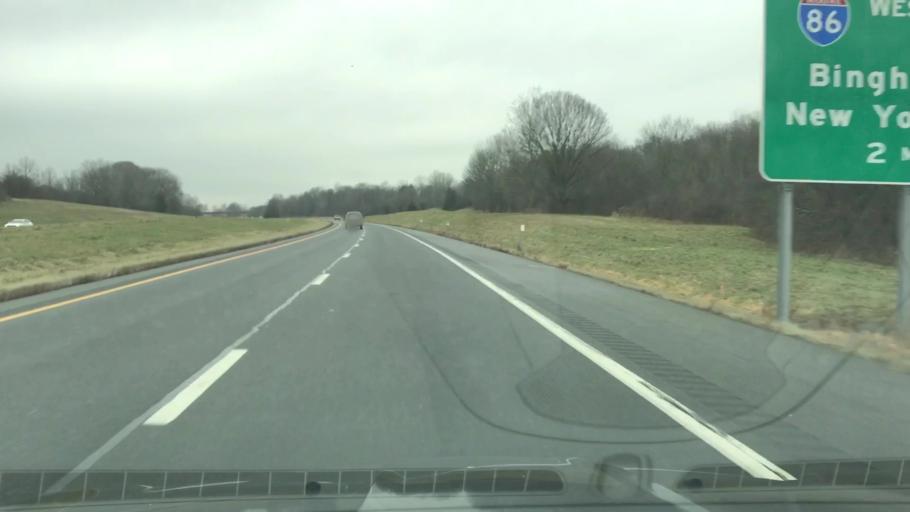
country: US
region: New York
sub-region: Orange County
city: Scotchtown
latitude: 41.4671
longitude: -74.3331
